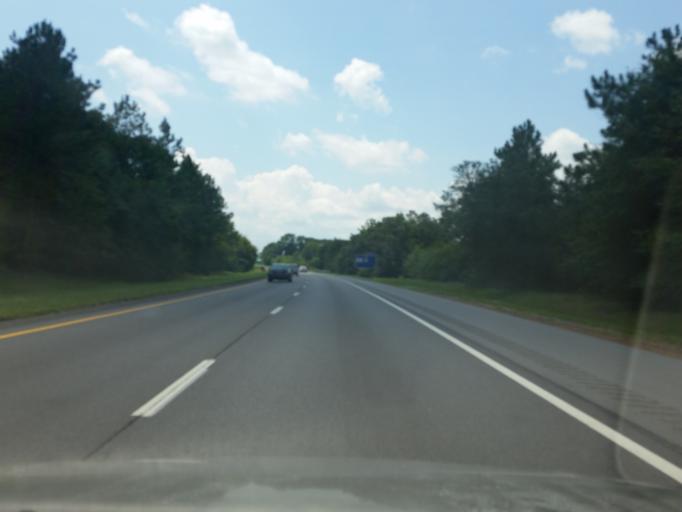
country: US
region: Alabama
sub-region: Baldwin County
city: Robertsdale
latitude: 30.6279
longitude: -87.6055
